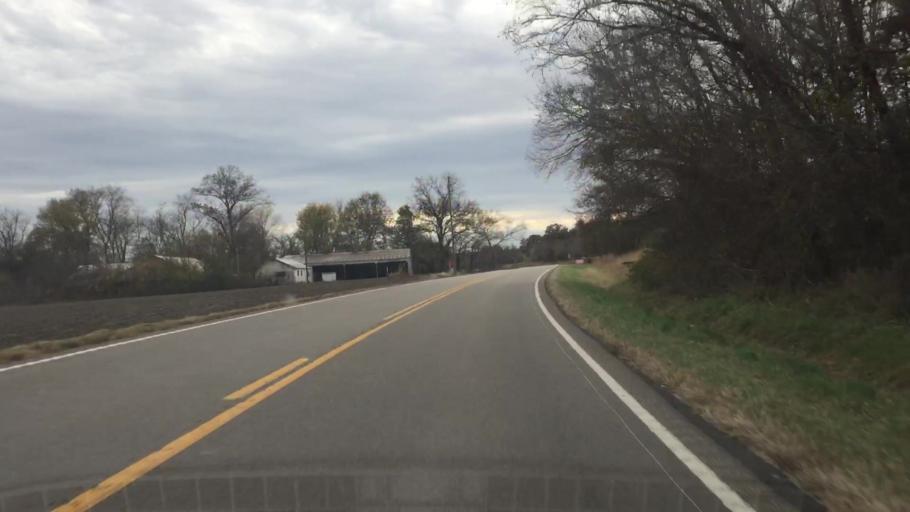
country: US
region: Missouri
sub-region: Callaway County
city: Holts Summit
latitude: 38.6120
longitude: -91.9767
